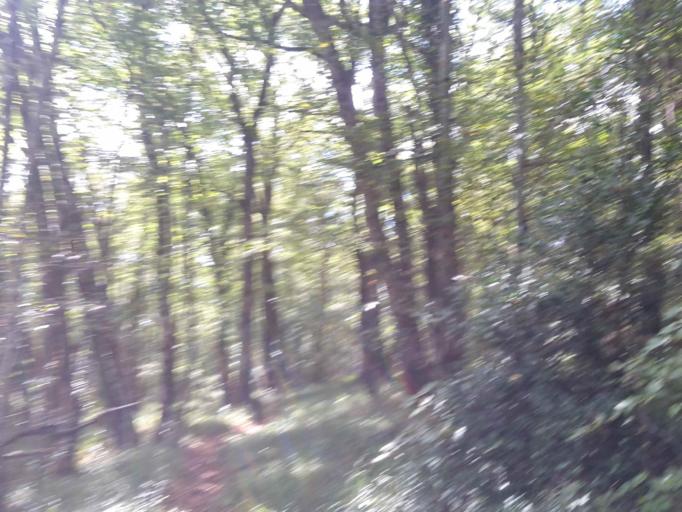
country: FR
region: Franche-Comte
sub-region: Departement du Doubs
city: Baume-les-Dames
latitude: 47.3445
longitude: 6.3817
